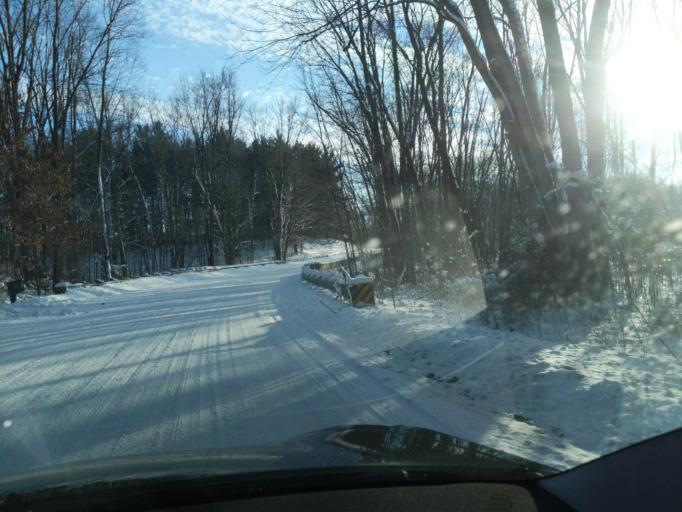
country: US
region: Michigan
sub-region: Ingham County
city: Stockbridge
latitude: 42.4368
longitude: -84.0751
